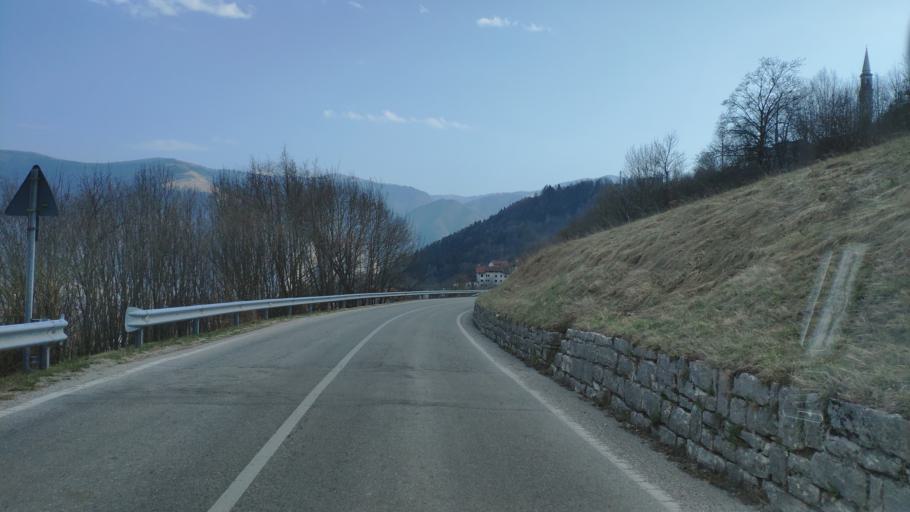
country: IT
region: Veneto
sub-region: Provincia di Vicenza
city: Enego
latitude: 45.9470
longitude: 11.7092
